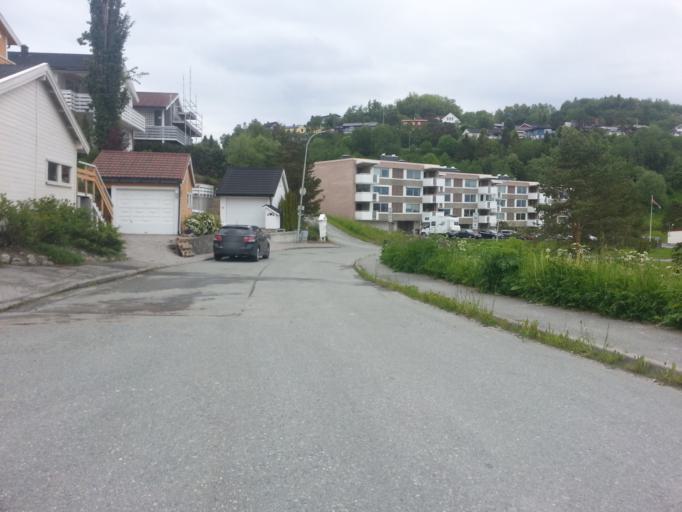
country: NO
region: Sor-Trondelag
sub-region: Trondheim
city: Trondheim
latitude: 63.4073
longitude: 10.4462
